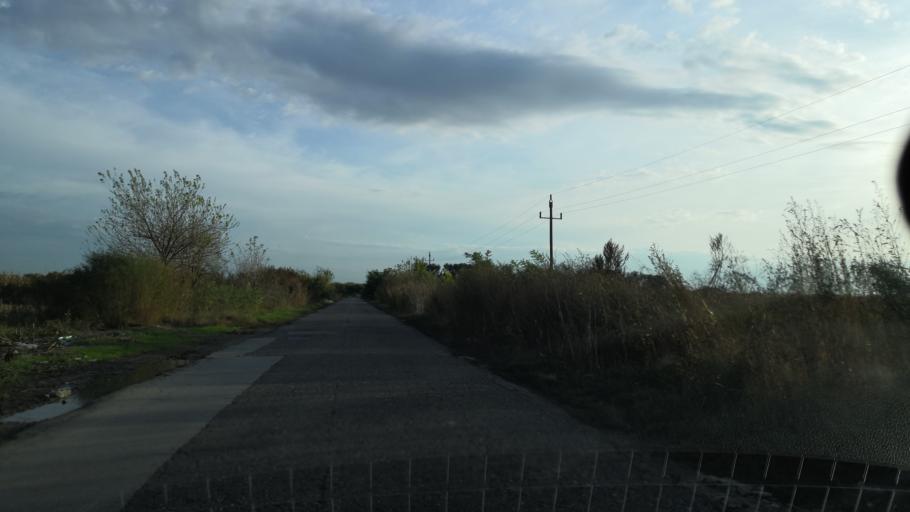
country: RS
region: Autonomna Pokrajina Vojvodina
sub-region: Sremski Okrug
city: Stara Pazova
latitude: 44.9999
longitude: 20.1649
